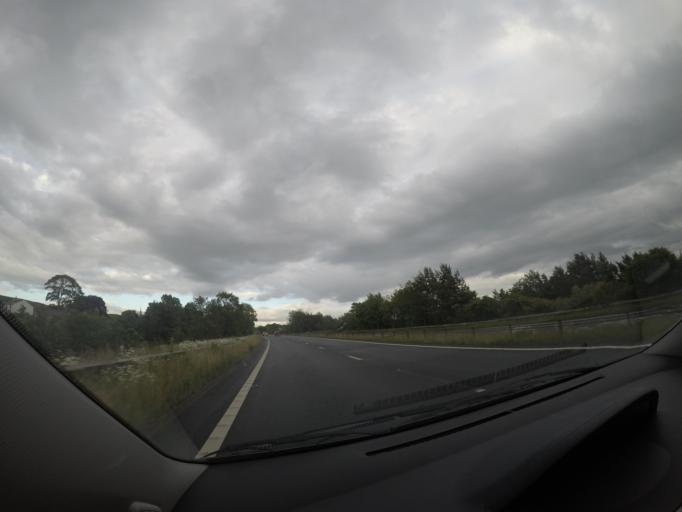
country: GB
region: England
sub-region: Cumbria
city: Kirkby Stephen
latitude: 54.5247
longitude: -2.3203
